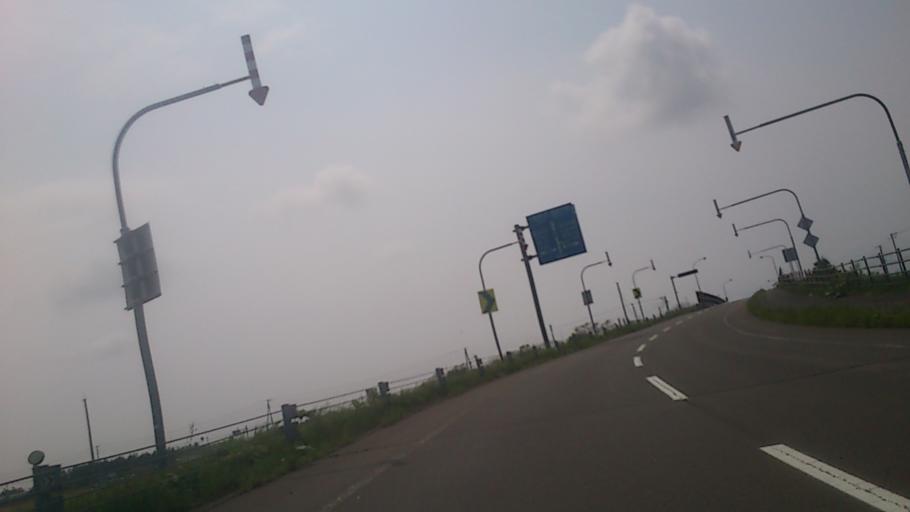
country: JP
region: Hokkaido
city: Nemuro
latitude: 43.2716
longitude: 145.5440
